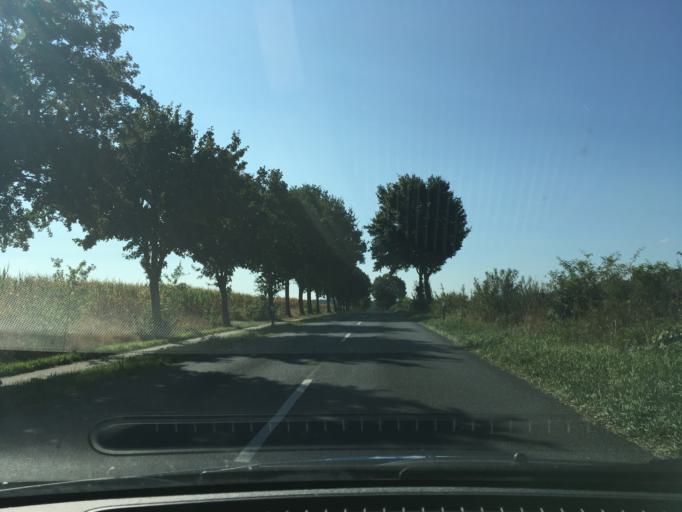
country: DE
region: Lower Saxony
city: Amelinghausen
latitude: 53.1187
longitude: 10.2163
